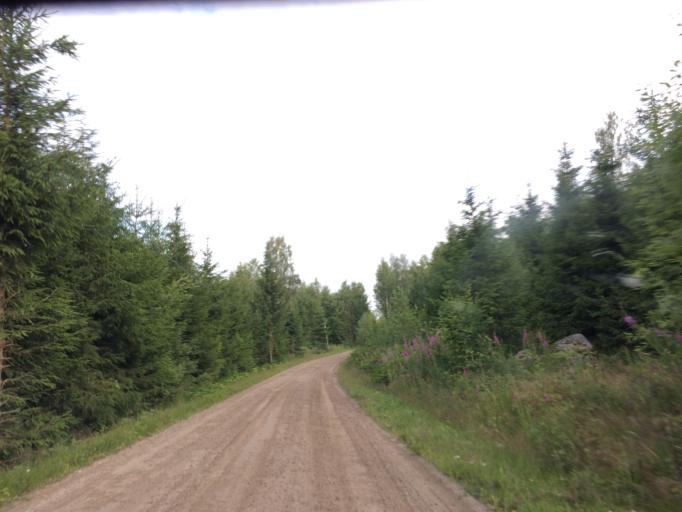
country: FI
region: Haeme
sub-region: Haemeenlinna
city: Janakkala
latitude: 60.8857
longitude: 24.6103
